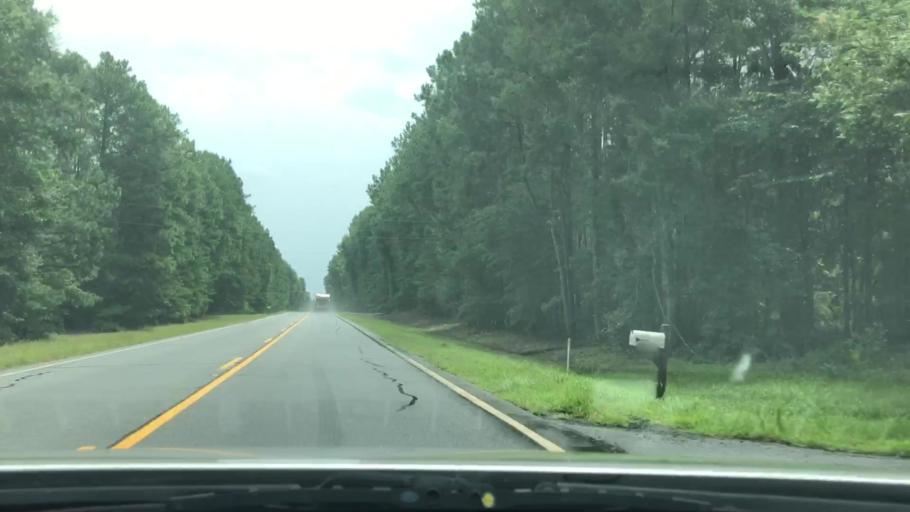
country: US
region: Georgia
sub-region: Pike County
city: Zebulon
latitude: 33.0830
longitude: -84.2642
